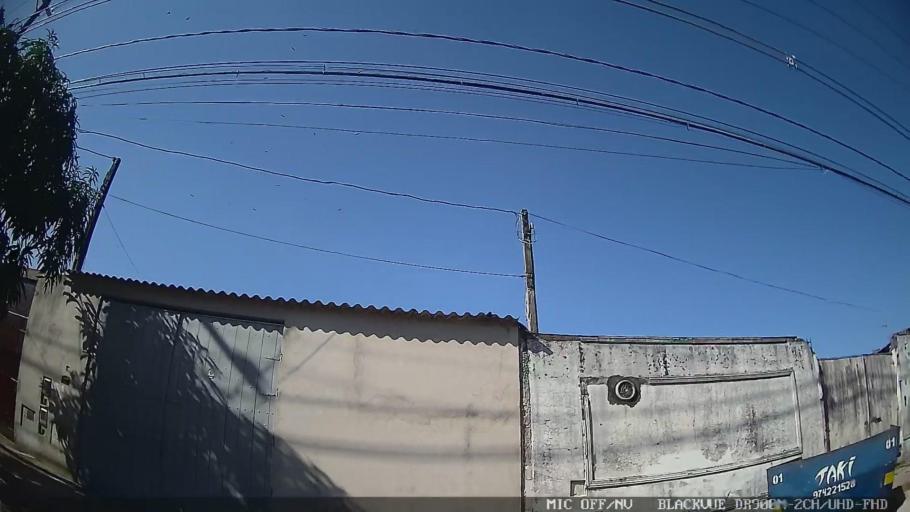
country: BR
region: Sao Paulo
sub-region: Guaruja
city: Guaruja
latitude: -23.9725
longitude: -46.2128
